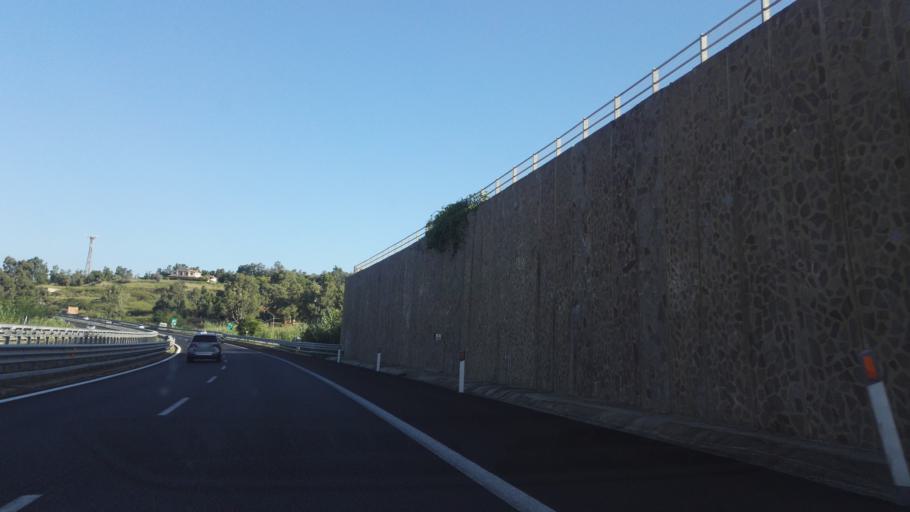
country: IT
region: Calabria
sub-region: Provincia di Catanzaro
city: Falerna Scalo
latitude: 38.9726
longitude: 16.1526
